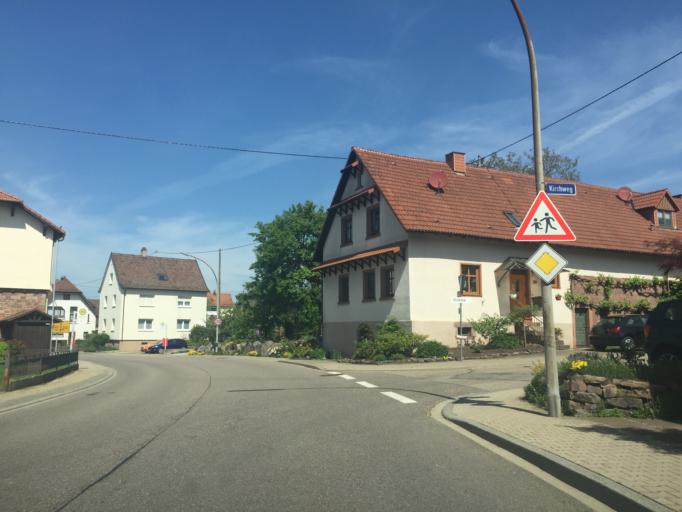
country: DE
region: Baden-Wuerttemberg
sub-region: Karlsruhe Region
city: Malsch
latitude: 48.8458
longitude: 8.3744
